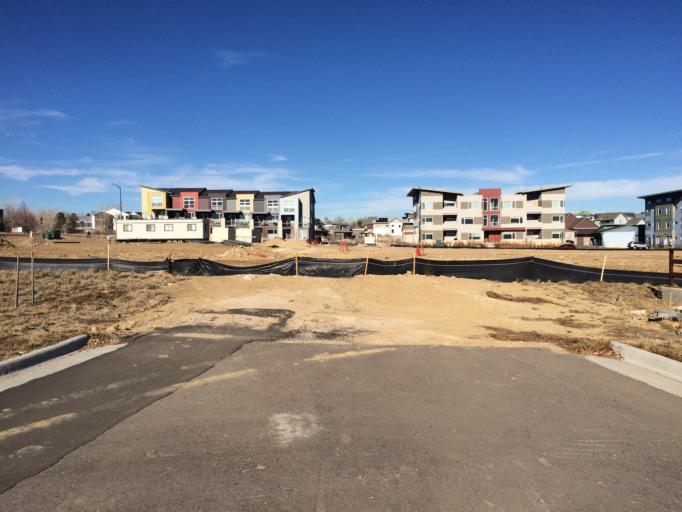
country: US
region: Colorado
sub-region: Boulder County
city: Louisville
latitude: 39.9871
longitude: -105.1214
